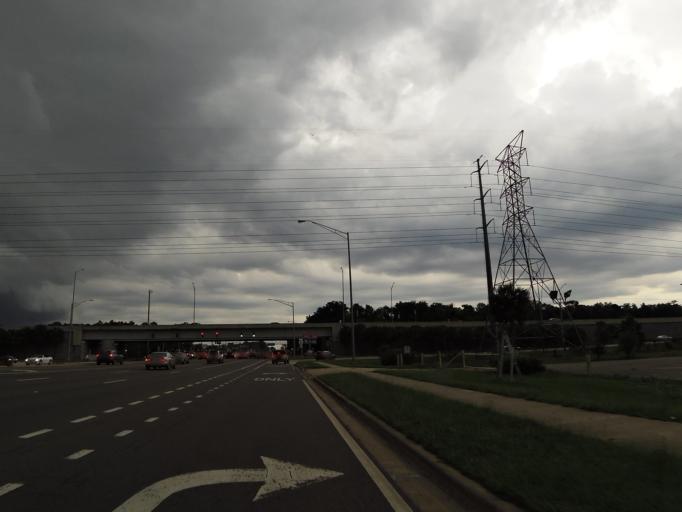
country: US
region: Florida
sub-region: Duval County
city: Neptune Beach
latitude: 30.2867
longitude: -81.5232
